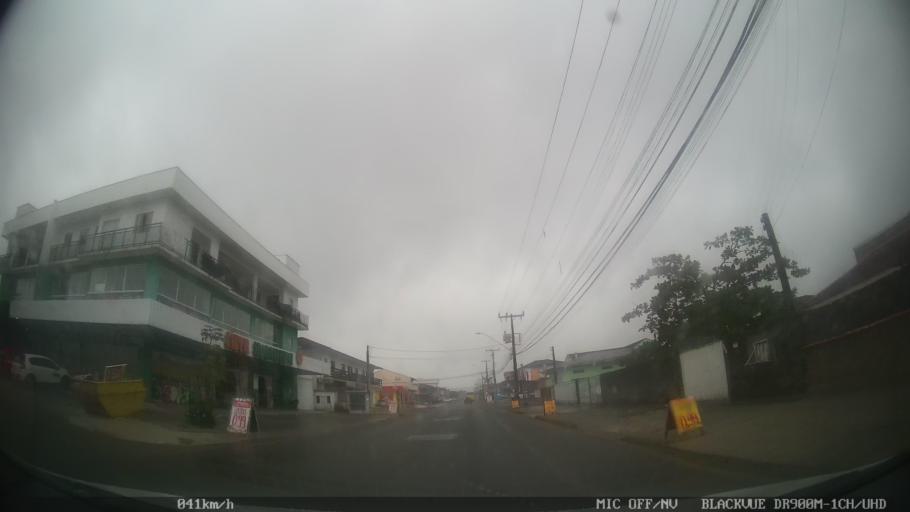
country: BR
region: Santa Catarina
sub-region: Joinville
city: Joinville
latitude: -26.2108
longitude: -48.8255
